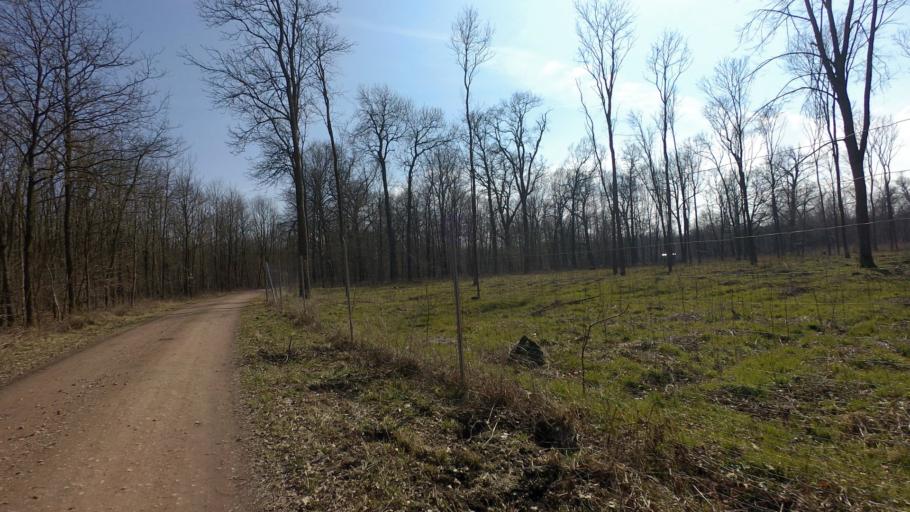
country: DE
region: Saxony-Anhalt
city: Vockerode
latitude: 51.8599
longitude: 12.3253
